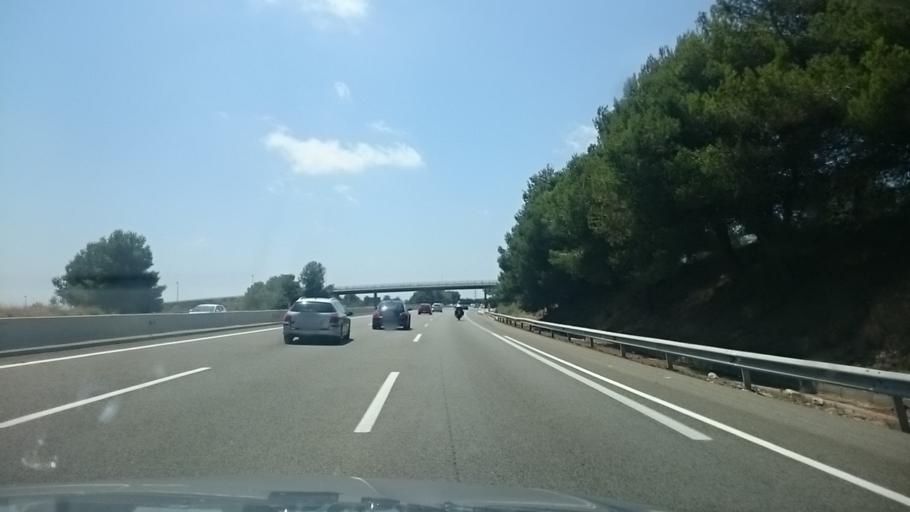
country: ES
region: Catalonia
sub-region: Provincia de Tarragona
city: El Vendrell
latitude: 41.2299
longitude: 1.5264
